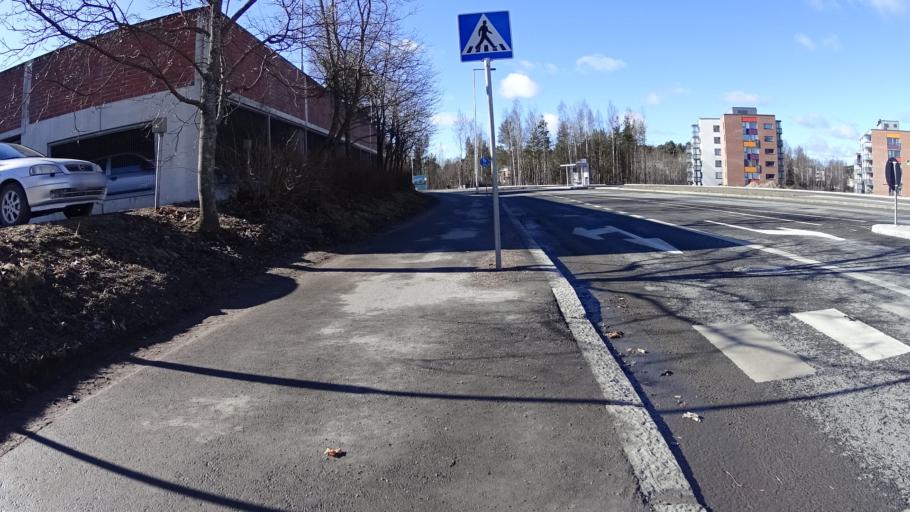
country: FI
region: Uusimaa
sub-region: Helsinki
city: Teekkarikylae
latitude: 60.2546
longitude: 24.8696
